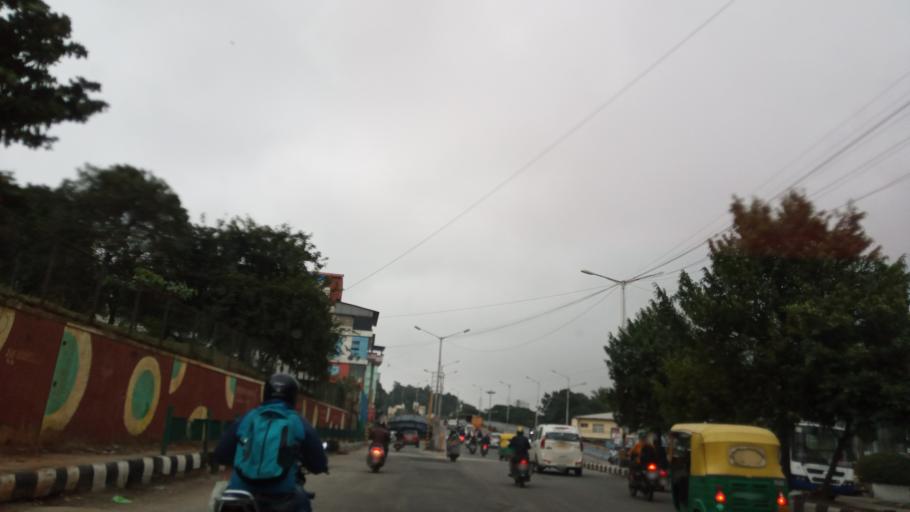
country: IN
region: Karnataka
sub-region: Bangalore Urban
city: Bangalore
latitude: 12.9224
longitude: 77.5582
